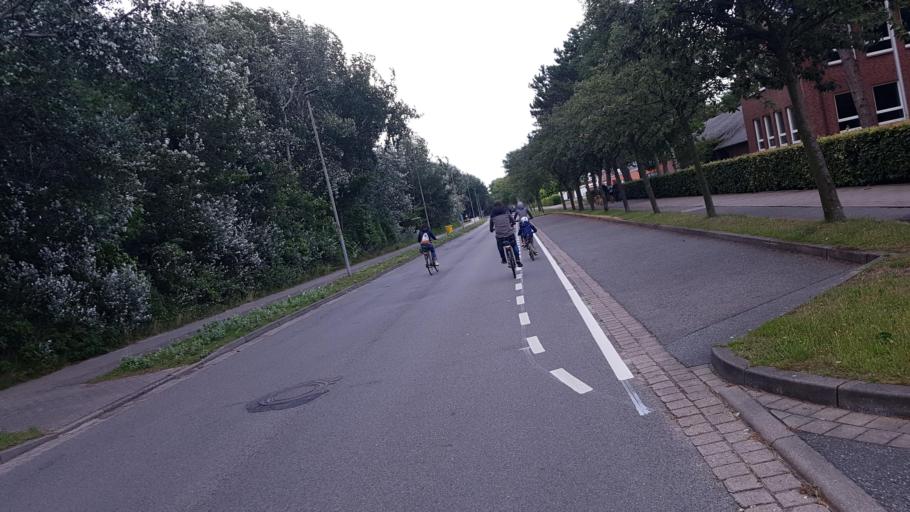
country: DE
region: Schleswig-Holstein
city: Sankt Peter-Ording
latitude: 54.2945
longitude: 8.6493
